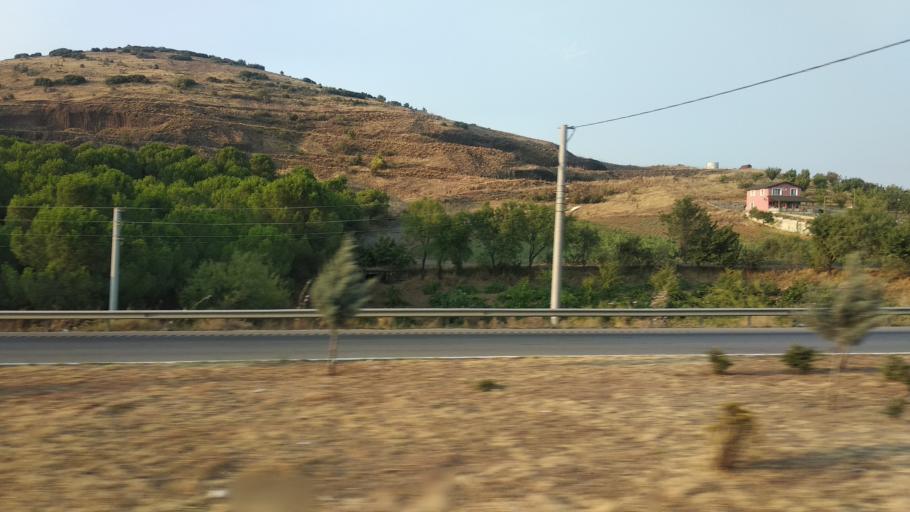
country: TR
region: Manisa
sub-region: Kula
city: Kula
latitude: 38.5678
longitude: 28.5780
